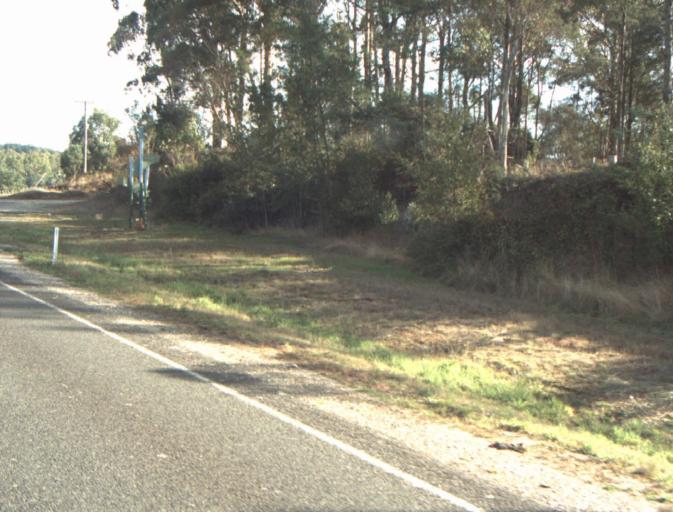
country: AU
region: Tasmania
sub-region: Launceston
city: Mayfield
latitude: -41.2856
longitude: 147.2182
